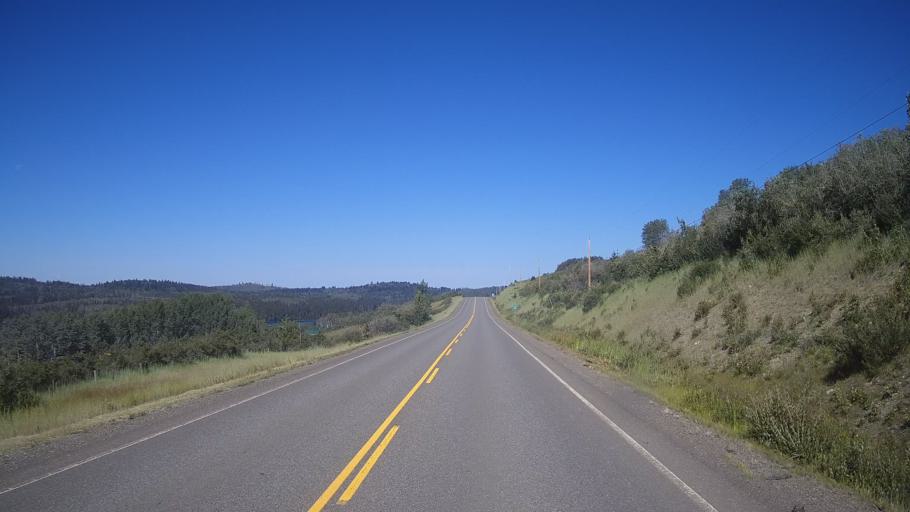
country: CA
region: British Columbia
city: Kamloops
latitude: 51.4969
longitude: -120.5837
